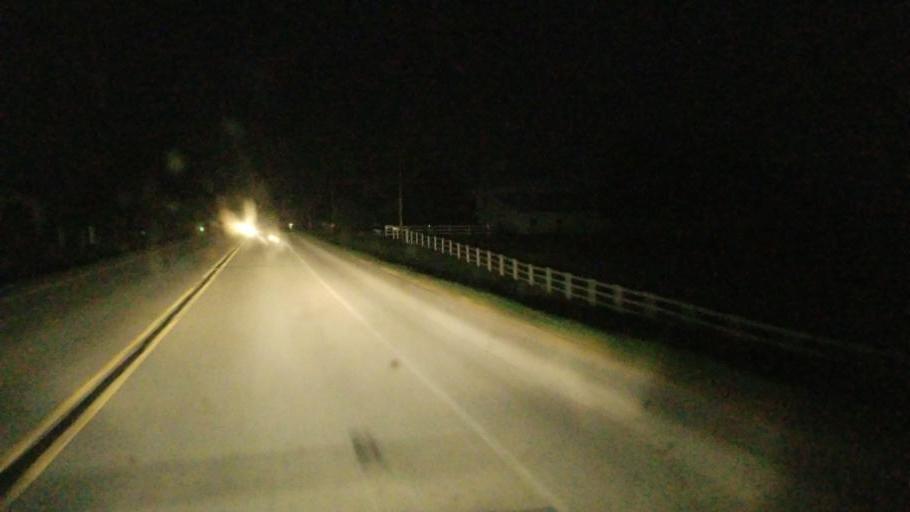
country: US
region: Indiana
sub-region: Elkhart County
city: Middlebury
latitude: 41.6760
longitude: -85.6227
